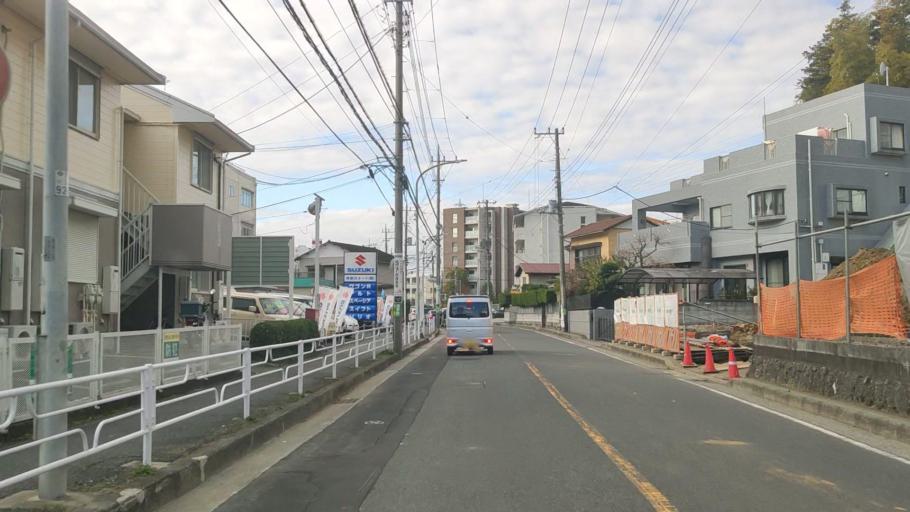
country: JP
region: Kanagawa
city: Yokohama
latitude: 35.4294
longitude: 139.5546
